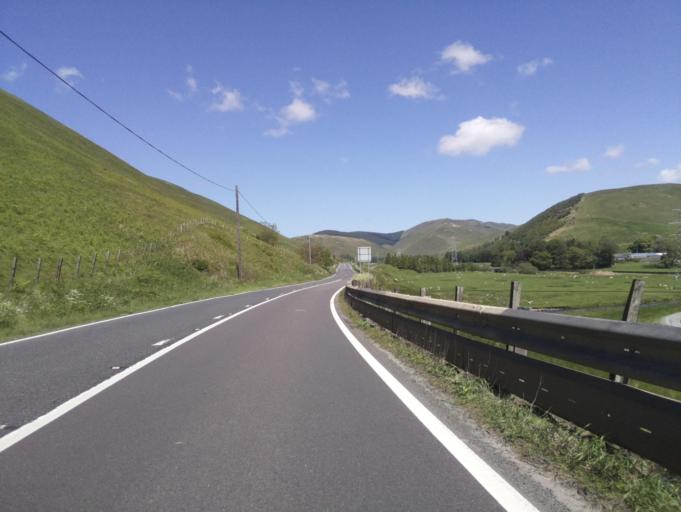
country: GB
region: Scotland
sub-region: Dumfries and Galloway
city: Langholm
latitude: 55.2404
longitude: -2.9720
